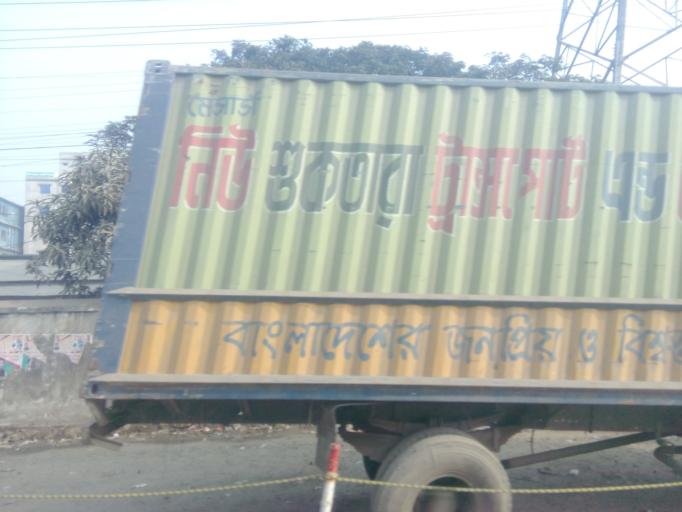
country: BD
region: Dhaka
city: Narayanganj
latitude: 23.7055
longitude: 90.5237
